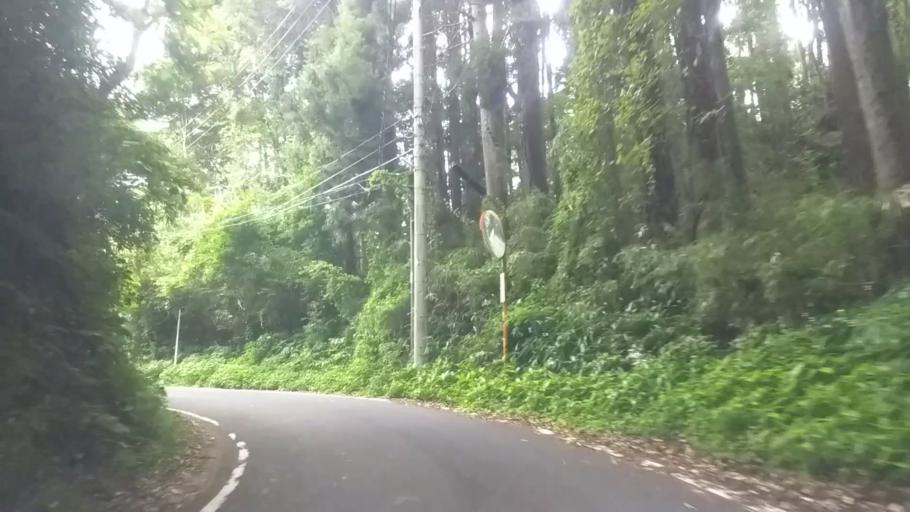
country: JP
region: Chiba
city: Kawaguchi
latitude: 35.2522
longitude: 140.0622
